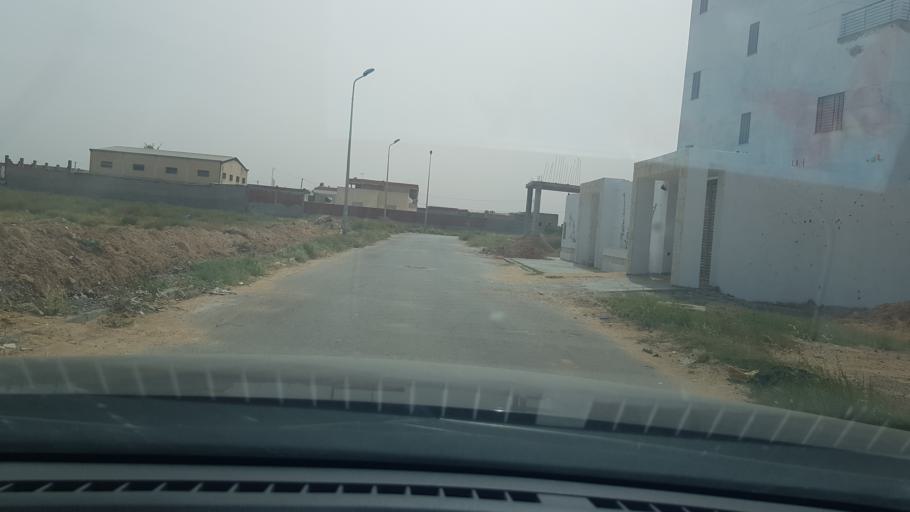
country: TN
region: Safaqis
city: Al Qarmadah
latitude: 34.8237
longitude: 10.7492
